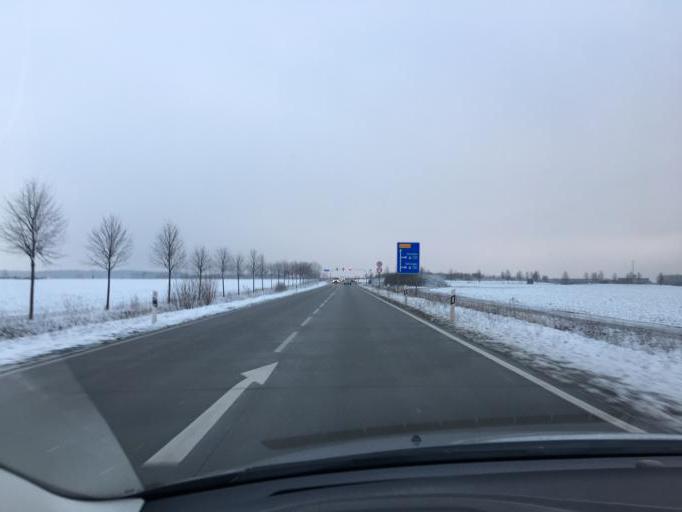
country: DE
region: Saxony
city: Grossposna
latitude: 51.2658
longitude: 12.4605
